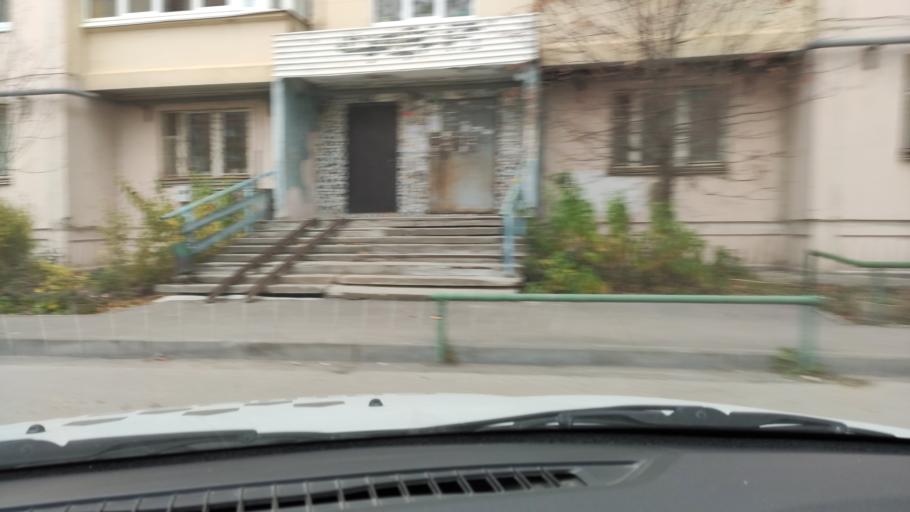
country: RU
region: Perm
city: Kondratovo
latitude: 57.9664
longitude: 56.1794
